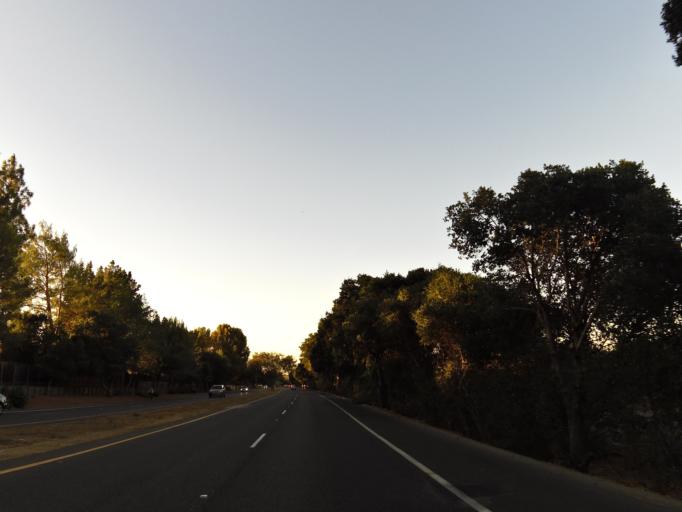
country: US
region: California
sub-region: Santa Clara County
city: Los Altos Hills
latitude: 37.3948
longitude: -122.1309
